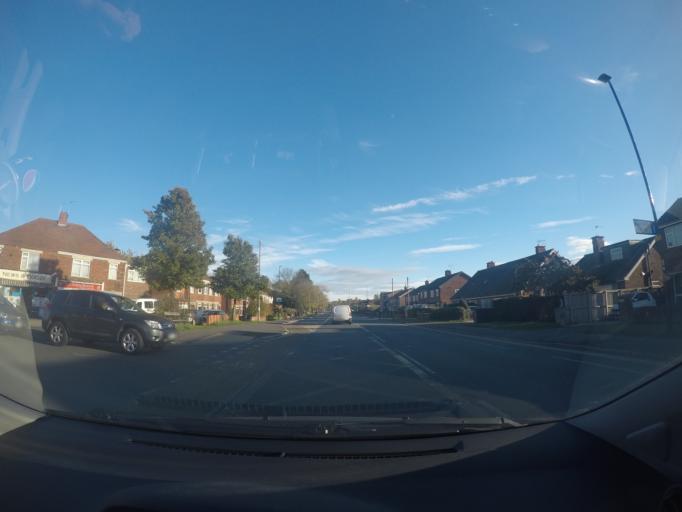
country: GB
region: England
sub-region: City of York
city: Nether Poppleton
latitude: 53.9664
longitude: -1.1262
